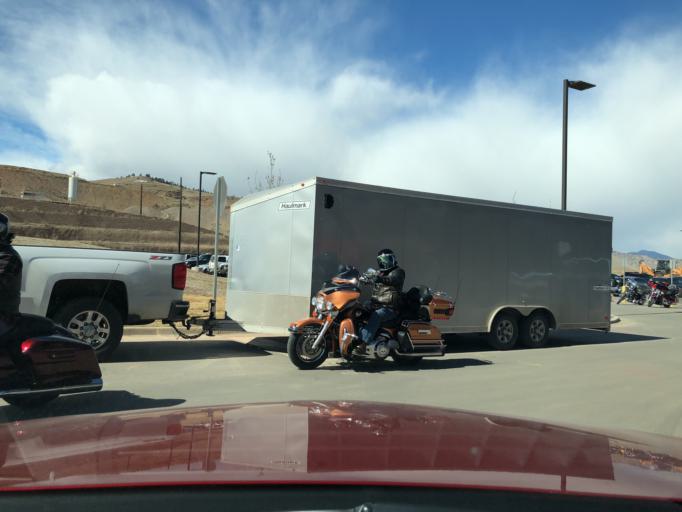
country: US
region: Colorado
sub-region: Jefferson County
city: West Pleasant View
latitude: 39.7047
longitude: -105.2053
